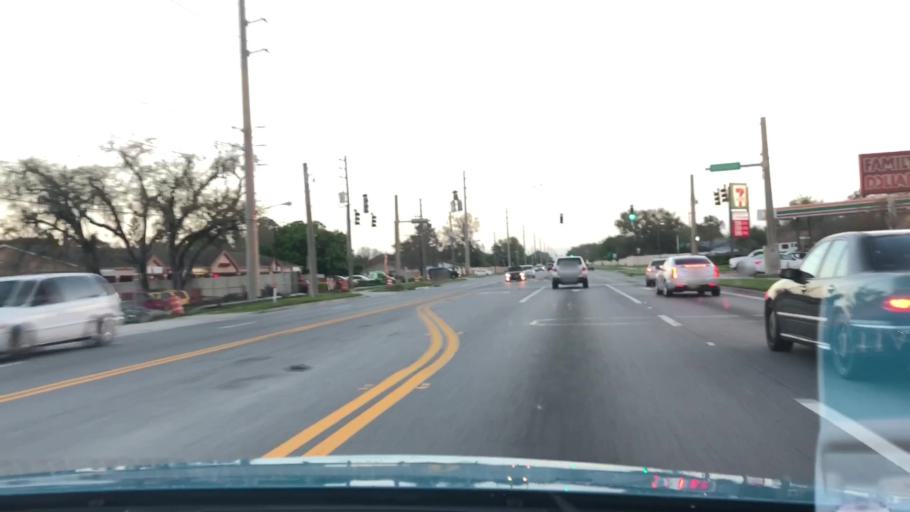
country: US
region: Florida
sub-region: Osceola County
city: Kissimmee
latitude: 28.3194
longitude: -81.3913
